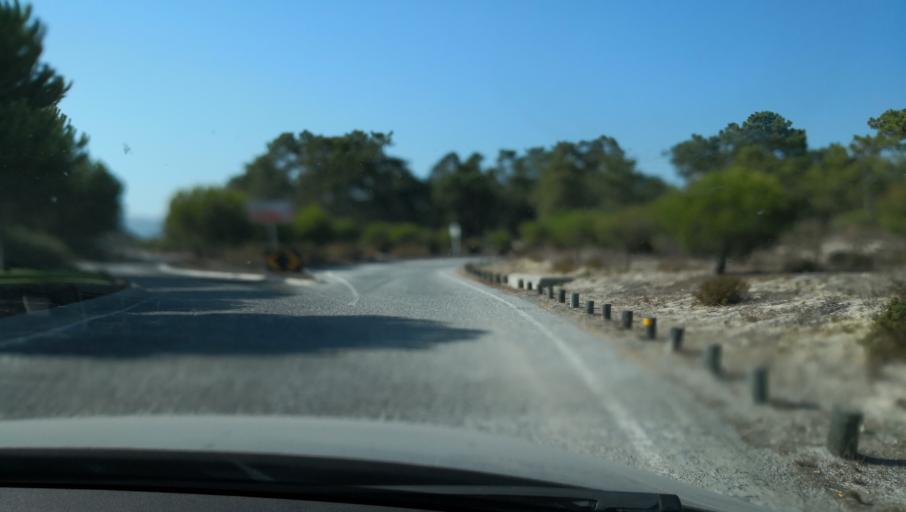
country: PT
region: Setubal
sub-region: Setubal
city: Setubal
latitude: 38.4648
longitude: -8.8701
